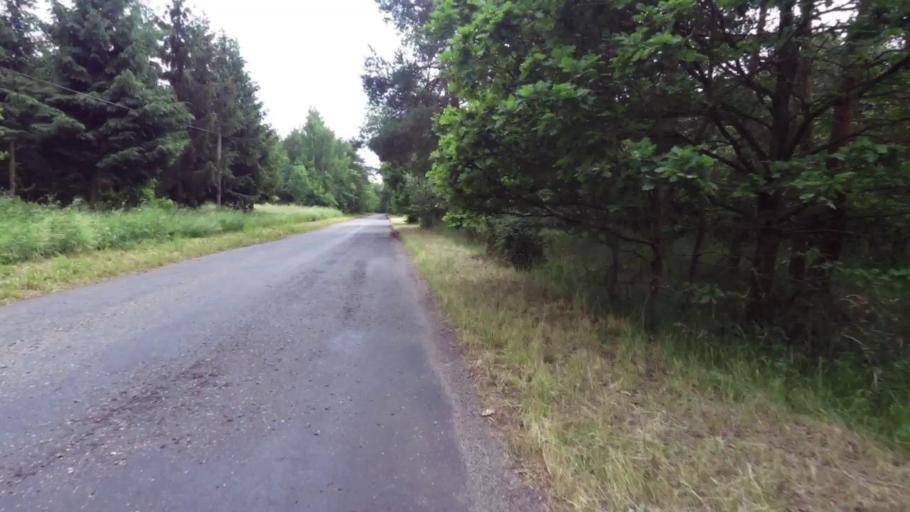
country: PL
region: West Pomeranian Voivodeship
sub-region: Powiat goleniowski
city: Stepnica
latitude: 53.7081
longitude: 14.5513
